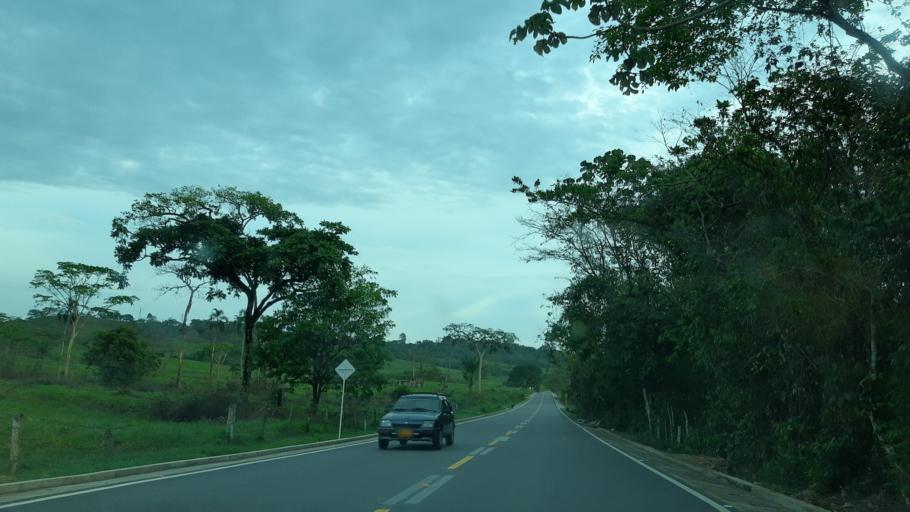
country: CO
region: Casanare
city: Sabanalarga
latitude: 4.8158
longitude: -73.0634
